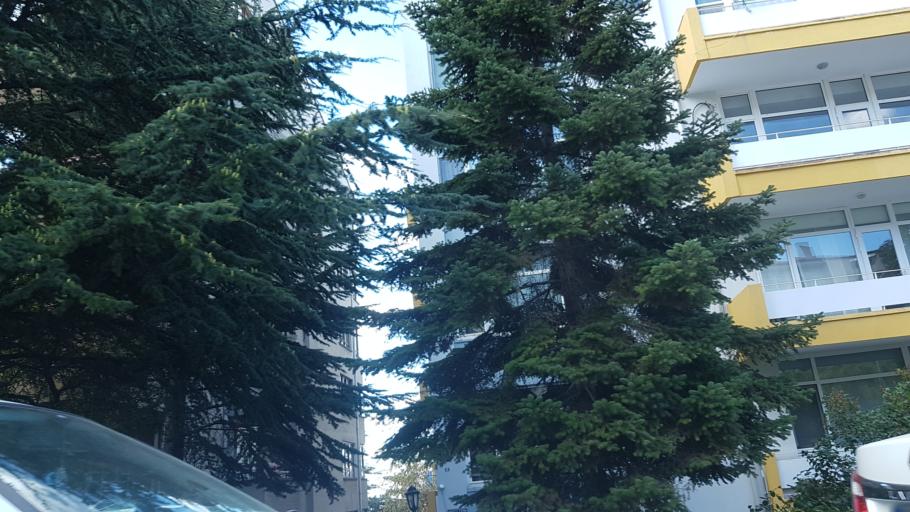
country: TR
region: Ankara
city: Cankaya
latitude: 39.9041
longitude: 32.8629
